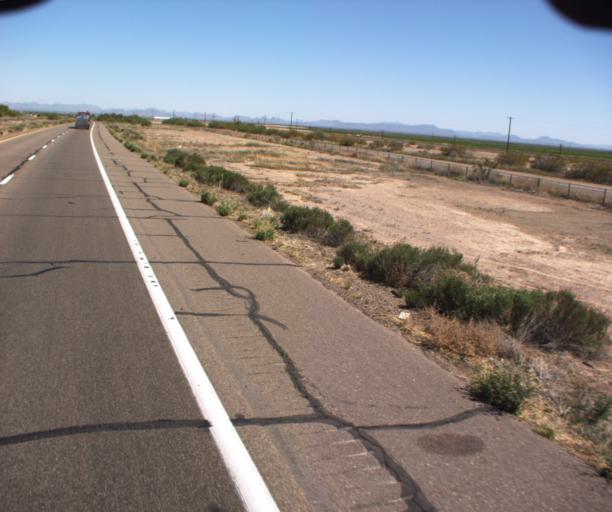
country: US
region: Arizona
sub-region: Maricopa County
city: Gila Bend
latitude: 32.9277
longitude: -112.8416
